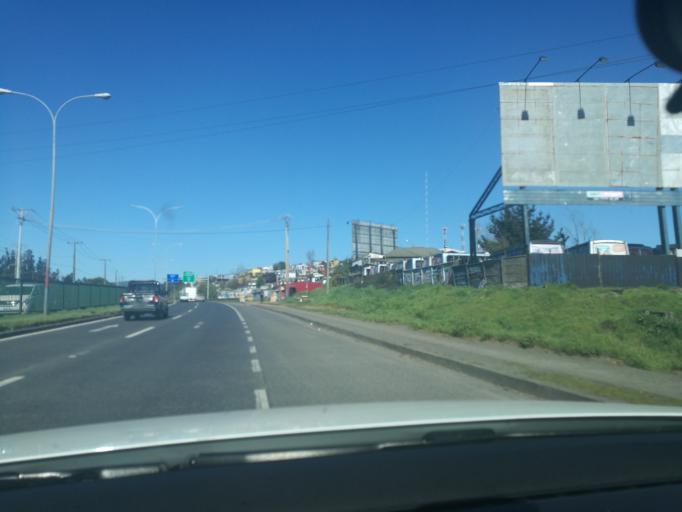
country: CL
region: Biobio
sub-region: Provincia de Concepcion
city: Concepcion
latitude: -36.8050
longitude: -73.0386
